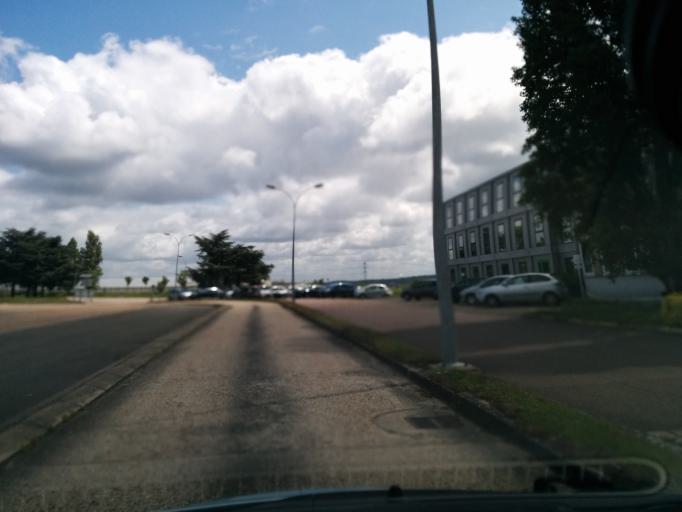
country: FR
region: Ile-de-France
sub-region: Departement des Yvelines
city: Mezieres-sur-Seine
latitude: 48.9731
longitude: 1.7960
